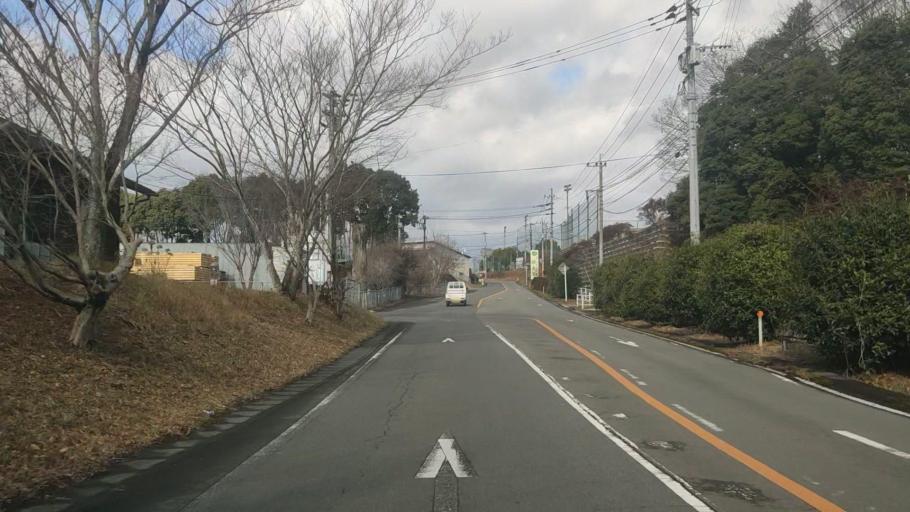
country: JP
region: Kumamoto
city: Hitoyoshi
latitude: 32.2345
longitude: 130.7958
